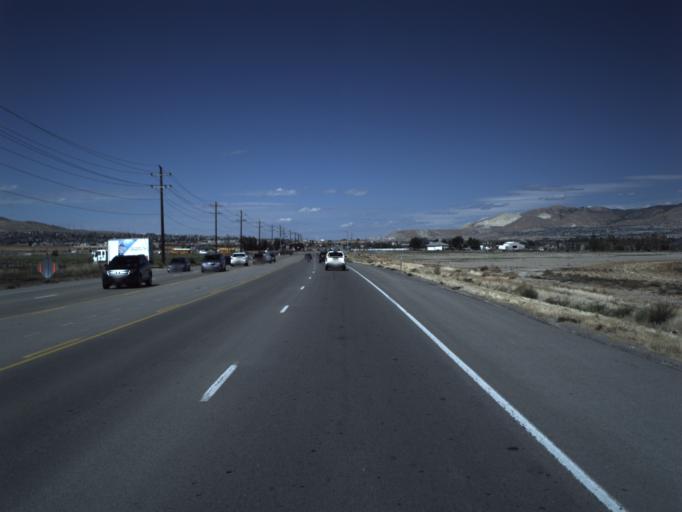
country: US
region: Utah
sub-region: Utah County
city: Saratoga Springs
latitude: 40.3655
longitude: -111.9162
